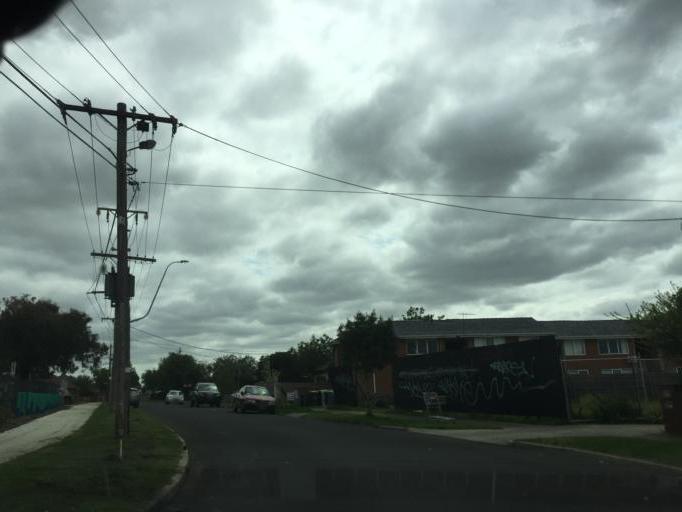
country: AU
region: Victoria
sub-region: Brimbank
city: Brooklyn
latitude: -37.8225
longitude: 144.8475
